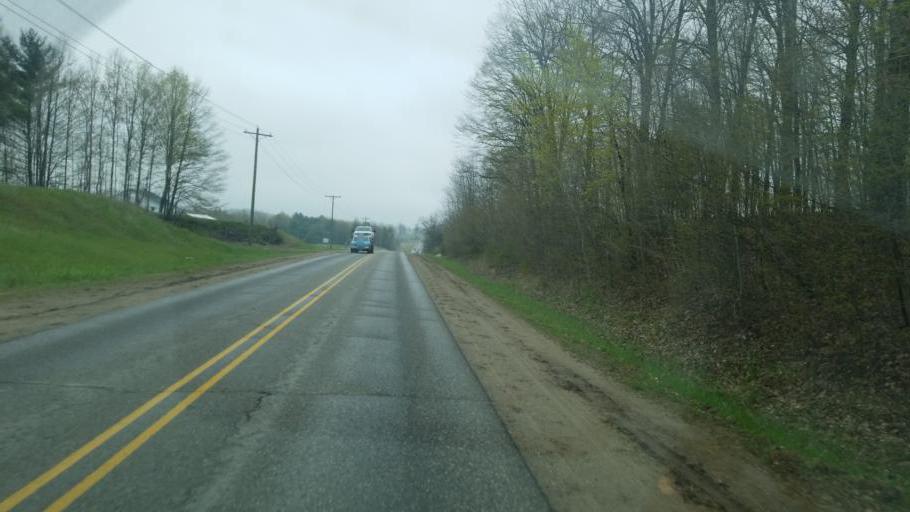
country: US
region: Michigan
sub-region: Mecosta County
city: Canadian Lakes
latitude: 43.5424
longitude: -85.3843
